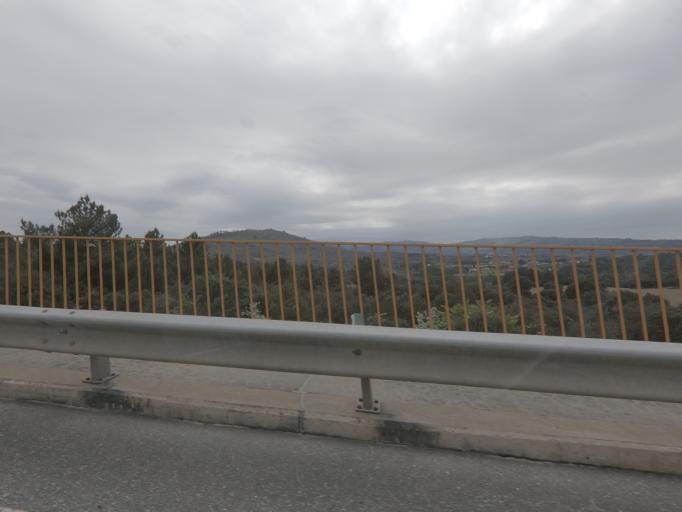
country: PT
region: Guarda
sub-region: Celorico da Beira
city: Celorico da Beira
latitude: 40.6323
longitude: -7.3132
